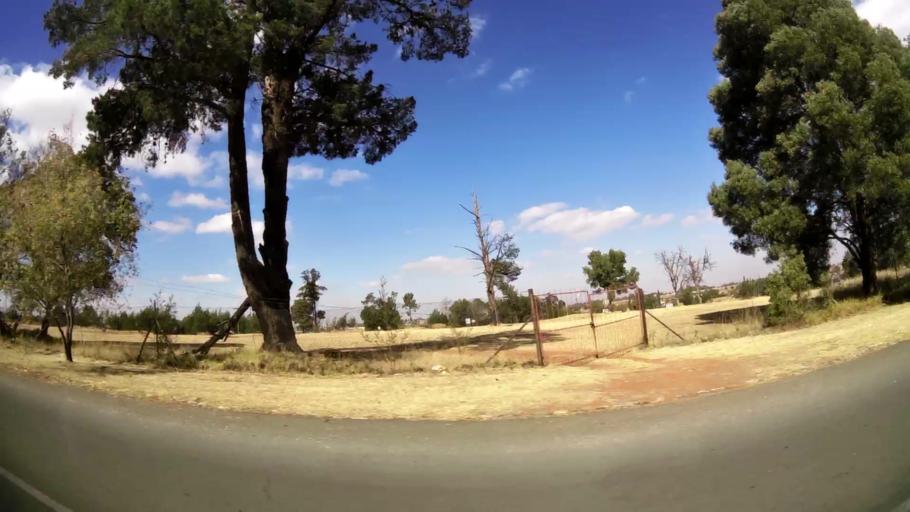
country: ZA
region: Gauteng
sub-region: West Rand District Municipality
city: Krugersdorp
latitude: -26.1075
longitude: 27.8004
